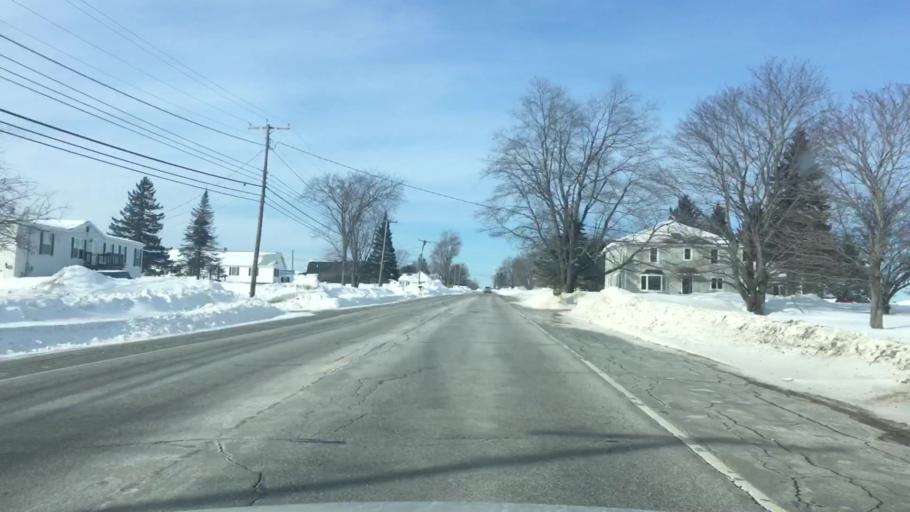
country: US
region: Maine
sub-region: Penobscot County
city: Charleston
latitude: 45.0226
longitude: -69.0294
